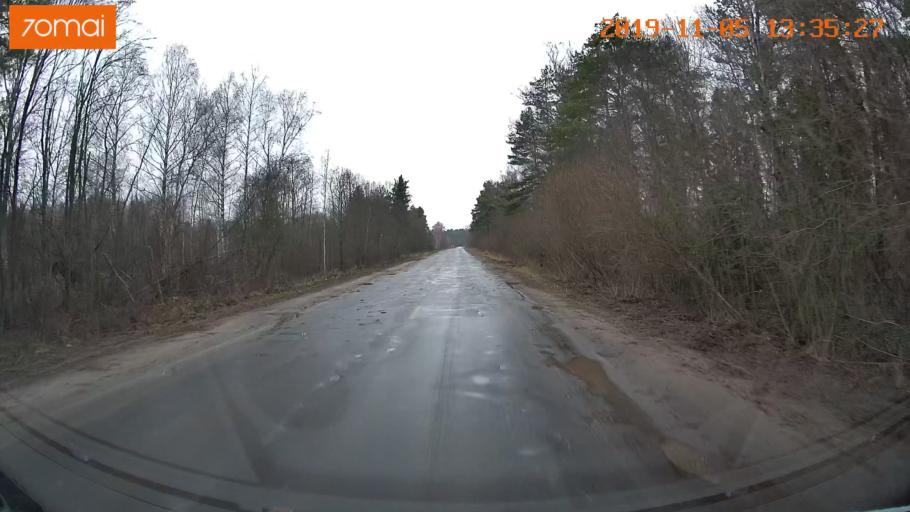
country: RU
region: Ivanovo
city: Shuya
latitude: 56.9079
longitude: 41.3872
